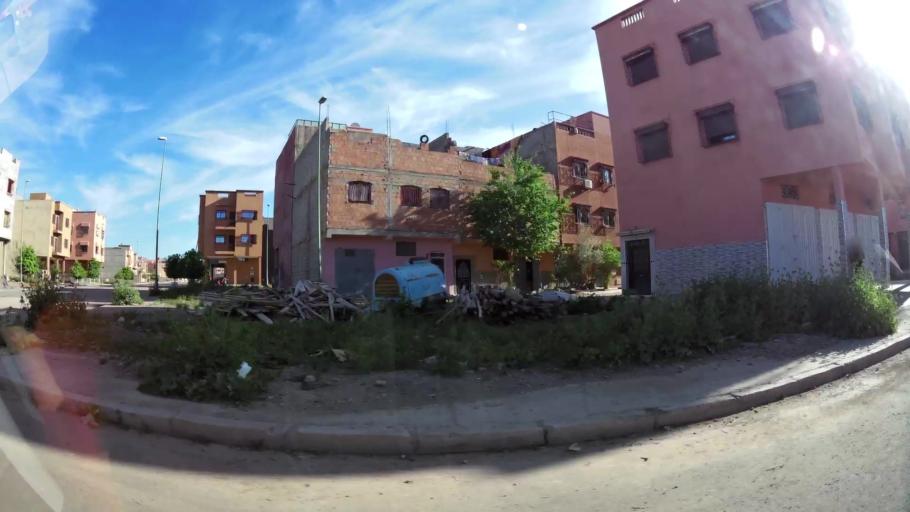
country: MA
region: Marrakech-Tensift-Al Haouz
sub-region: Marrakech
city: Marrakesh
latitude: 31.6900
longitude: -8.0654
